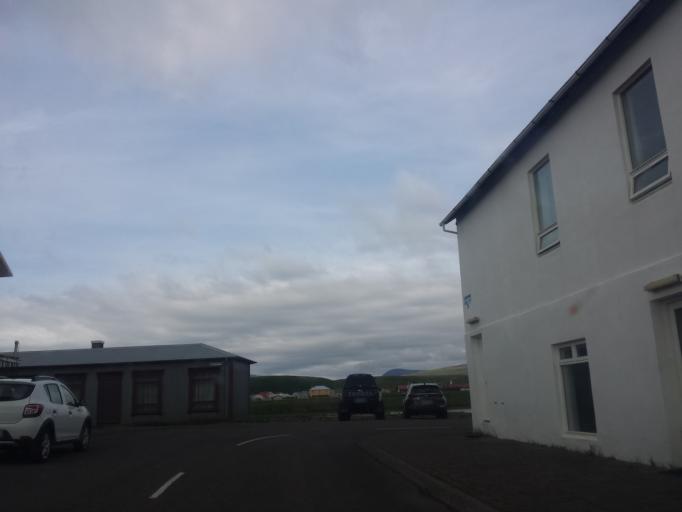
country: IS
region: Northwest
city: Saudarkrokur
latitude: 65.6600
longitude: -20.3007
